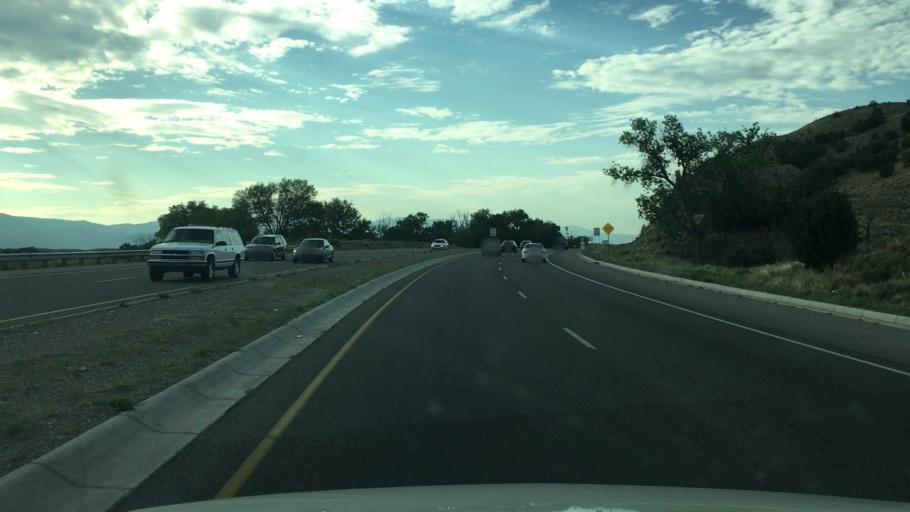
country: US
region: New Mexico
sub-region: Rio Arriba County
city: Espanola
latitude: 35.9848
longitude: -106.0518
